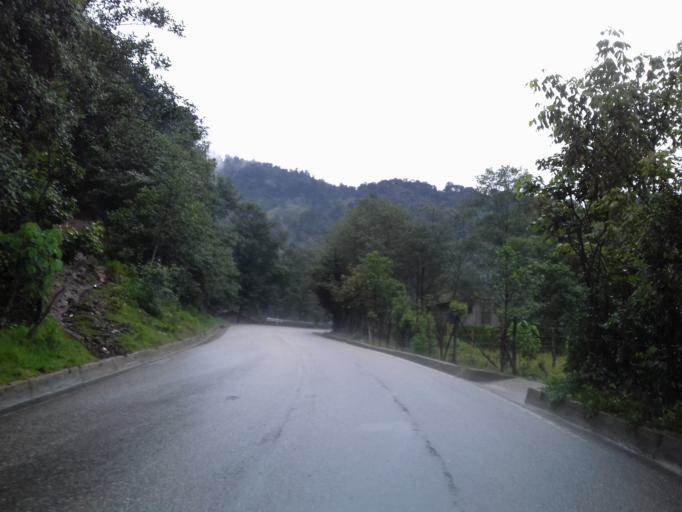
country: GT
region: Quiche
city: Nebaj
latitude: 15.3825
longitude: -91.1108
